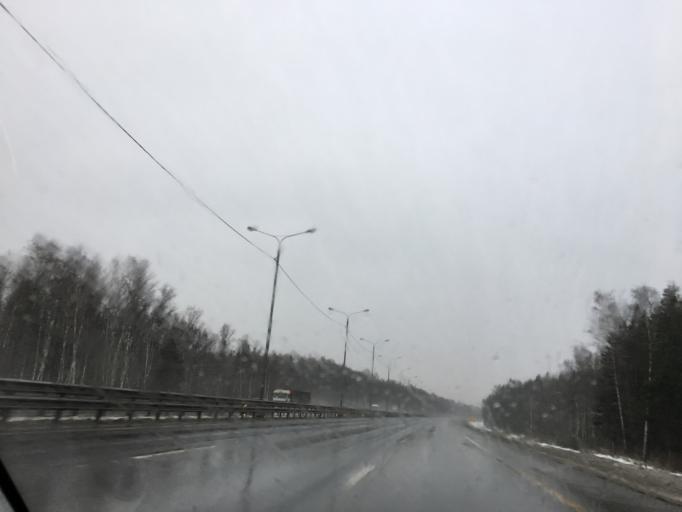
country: RU
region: Moskovskaya
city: Novyy Byt
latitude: 55.1080
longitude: 37.5818
